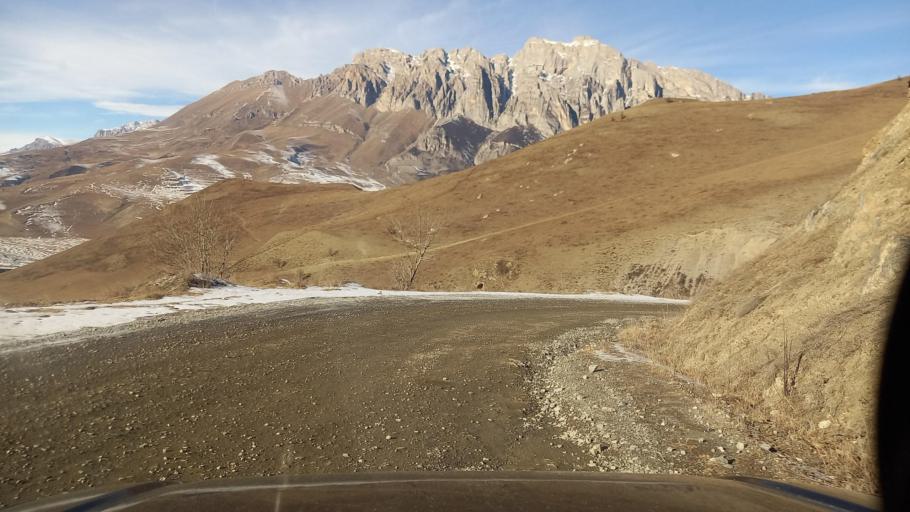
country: RU
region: North Ossetia
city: Verkhniy Fiagdon
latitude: 42.8388
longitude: 44.4645
